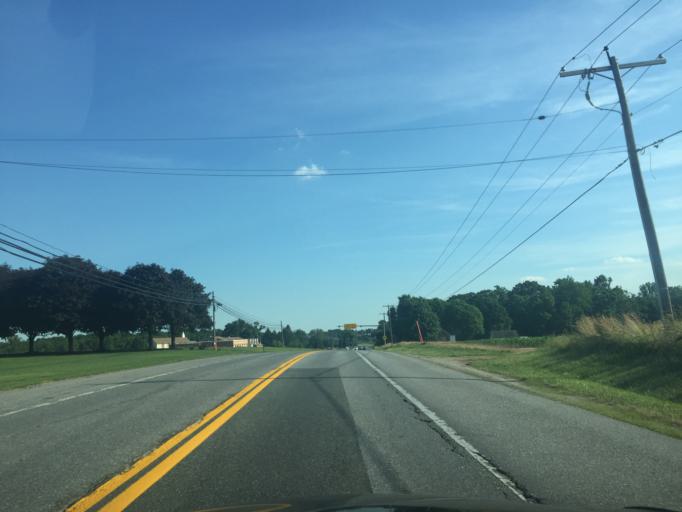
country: US
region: Maryland
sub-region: Harford County
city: Jarrettsville
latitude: 39.6172
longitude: -76.4766
